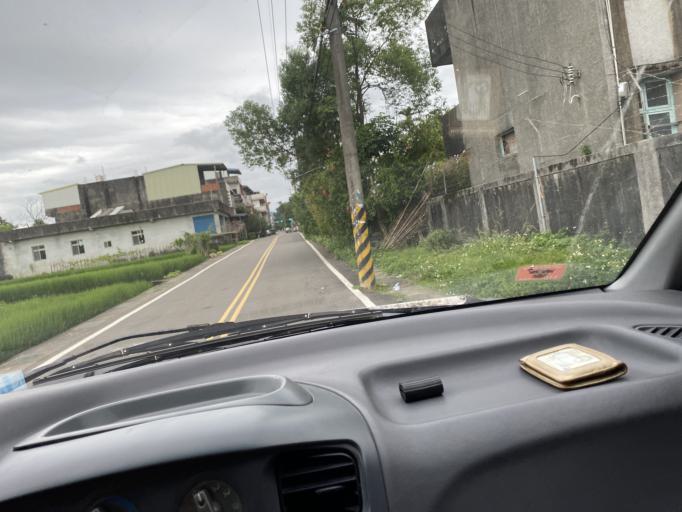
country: TW
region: Taiwan
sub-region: Hsinchu
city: Zhubei
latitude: 24.7195
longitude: 121.1136
